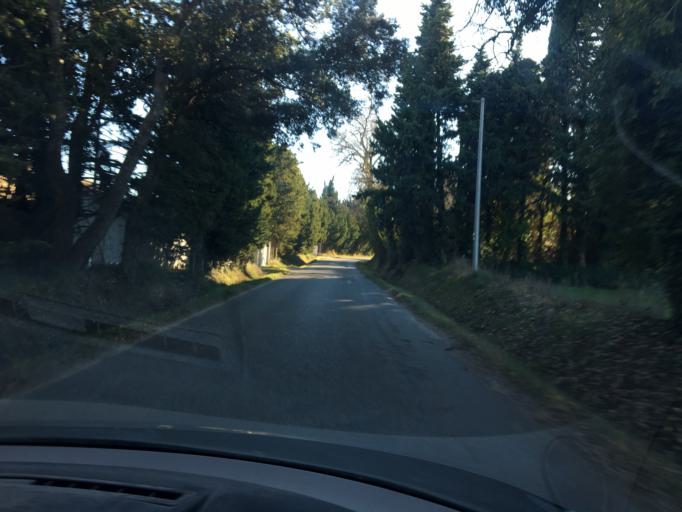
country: FR
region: Provence-Alpes-Cote d'Azur
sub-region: Departement des Bouches-du-Rhone
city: Saint-Remy-de-Provence
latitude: 43.7869
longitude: 4.7920
